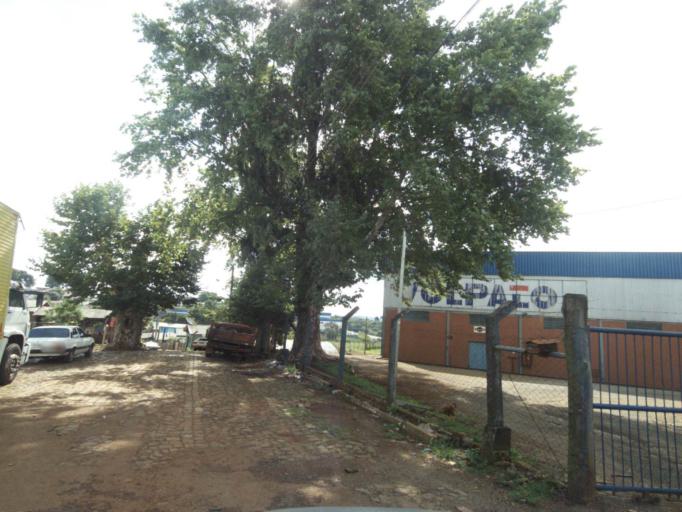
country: BR
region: Rio Grande do Sul
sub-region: Lagoa Vermelha
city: Lagoa Vermelha
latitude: -28.2076
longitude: -51.5344
